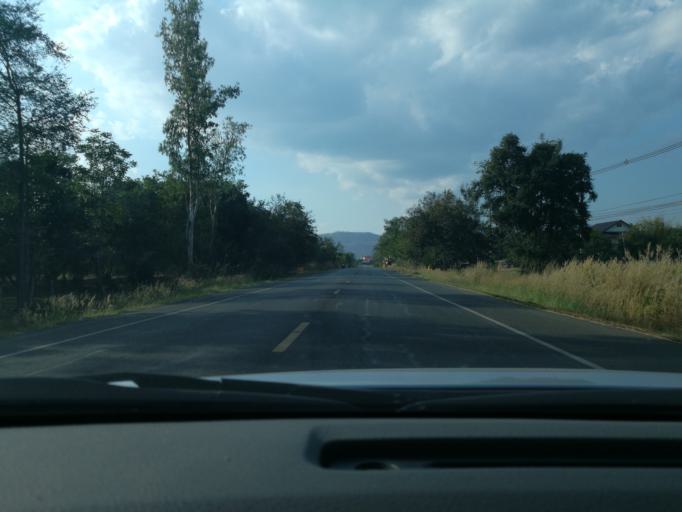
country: TH
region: Phetchabun
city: Phetchabun
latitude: 16.5434
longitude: 101.1457
